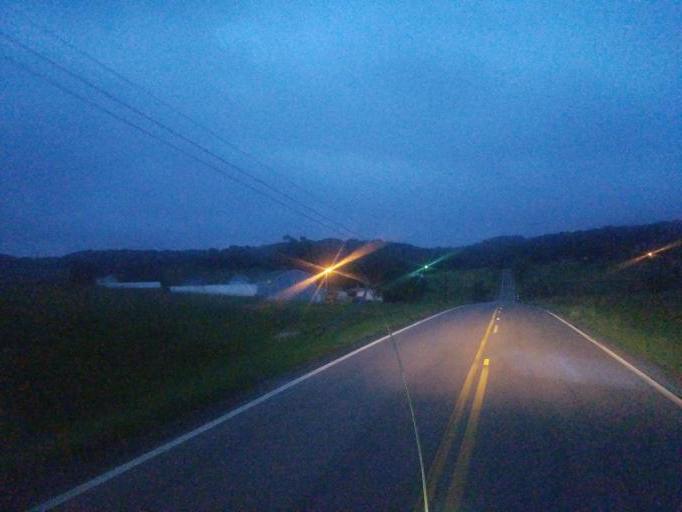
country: US
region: Ohio
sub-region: Carroll County
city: Carrollton
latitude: 40.5957
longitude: -81.0186
